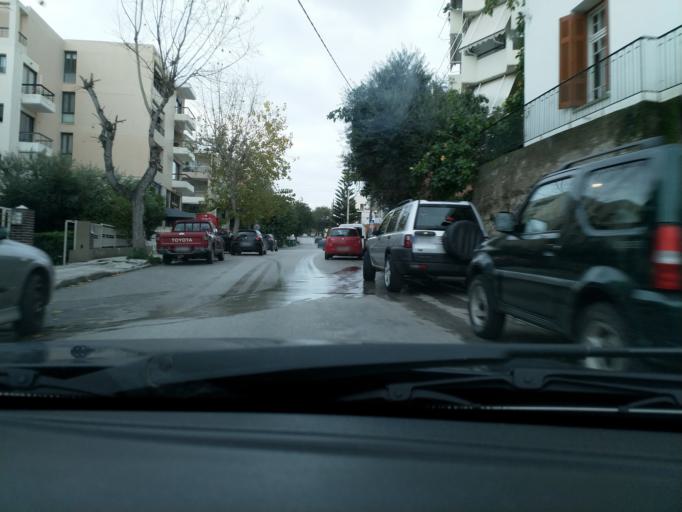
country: GR
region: Crete
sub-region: Nomos Chanias
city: Chania
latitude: 35.5103
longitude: 24.0348
